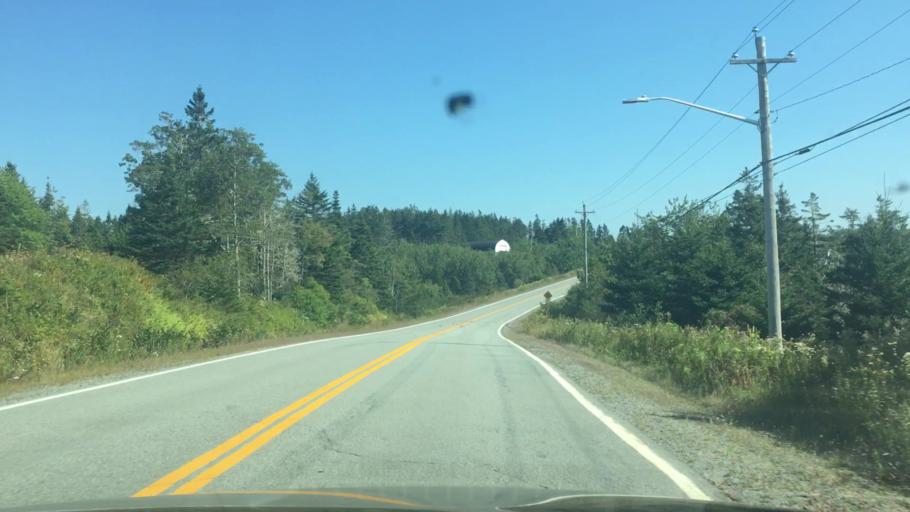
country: CA
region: Nova Scotia
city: New Glasgow
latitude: 44.8252
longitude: -62.6294
